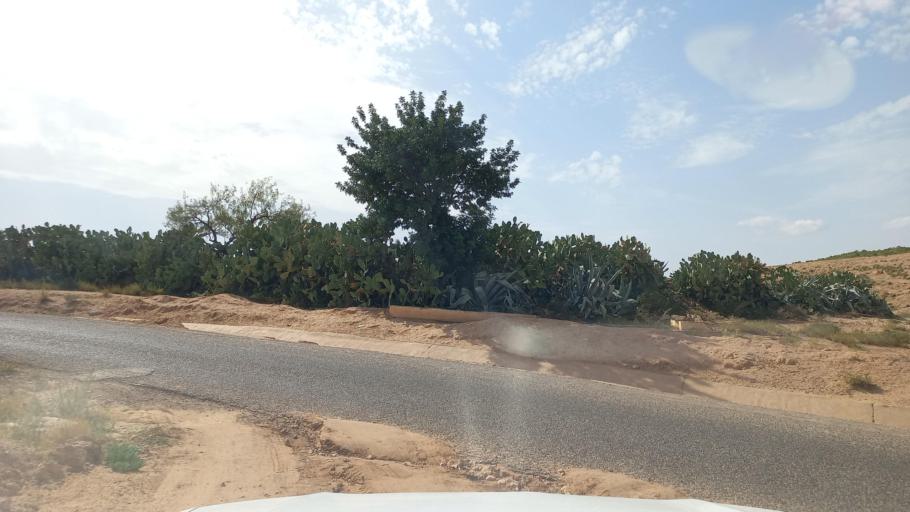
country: TN
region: Al Qasrayn
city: Kasserine
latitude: 35.3654
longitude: 8.8546
